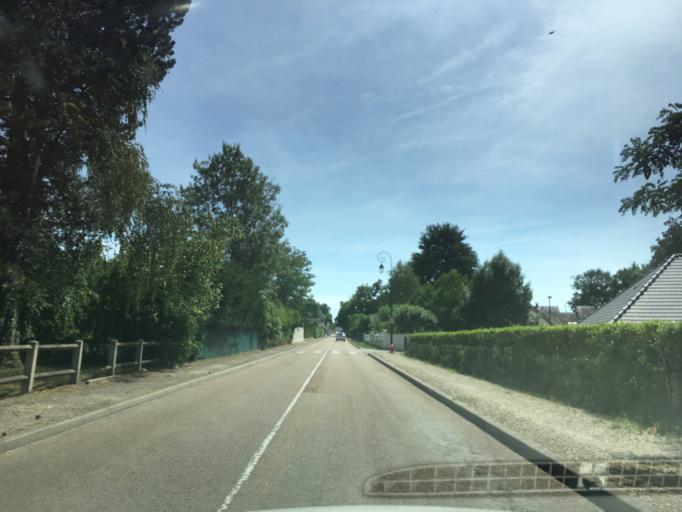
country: FR
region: Bourgogne
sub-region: Departement de l'Yonne
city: Saint-Georges-sur-Baulche
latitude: 47.8120
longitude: 3.5365
